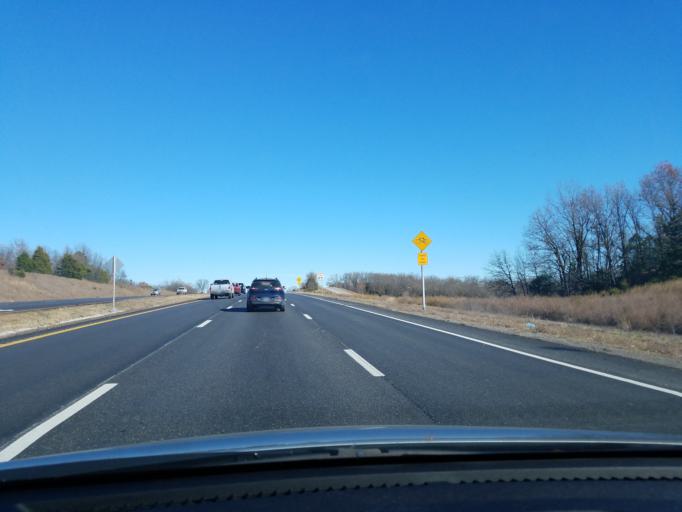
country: US
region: Missouri
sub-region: Taney County
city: Hollister
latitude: 36.5706
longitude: -93.2490
